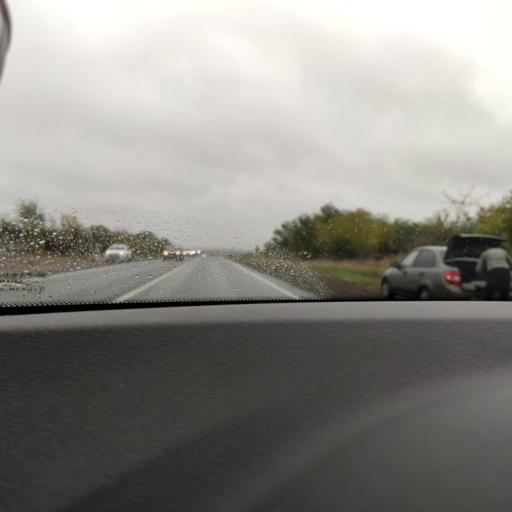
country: RU
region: Samara
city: Mirnyy
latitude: 53.6395
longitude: 50.2295
